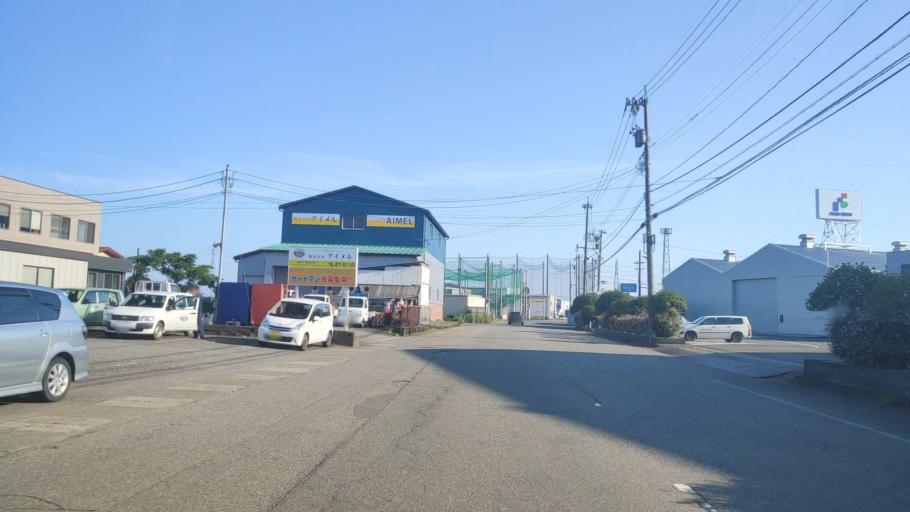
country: JP
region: Fukui
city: Fukui-shi
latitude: 36.0826
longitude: 136.2588
